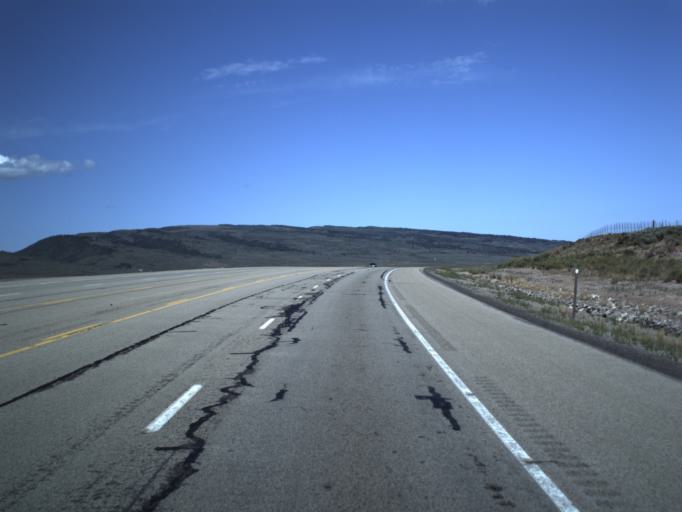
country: US
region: Utah
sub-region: Carbon County
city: Helper
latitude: 39.8458
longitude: -111.0030
